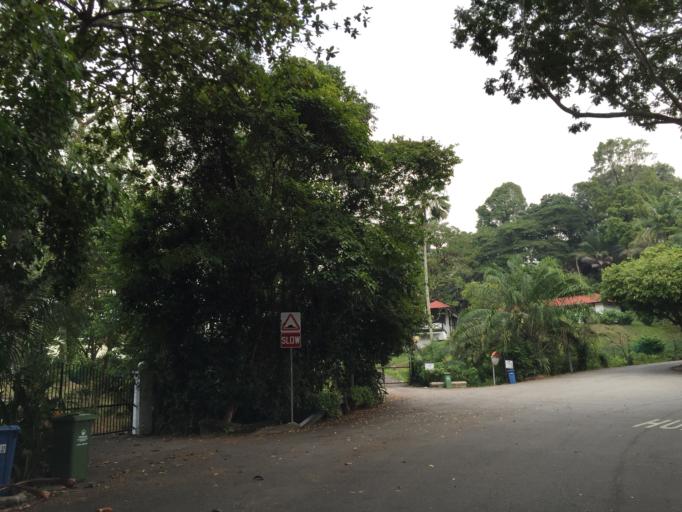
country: SG
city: Singapore
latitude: 1.3227
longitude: 103.8287
